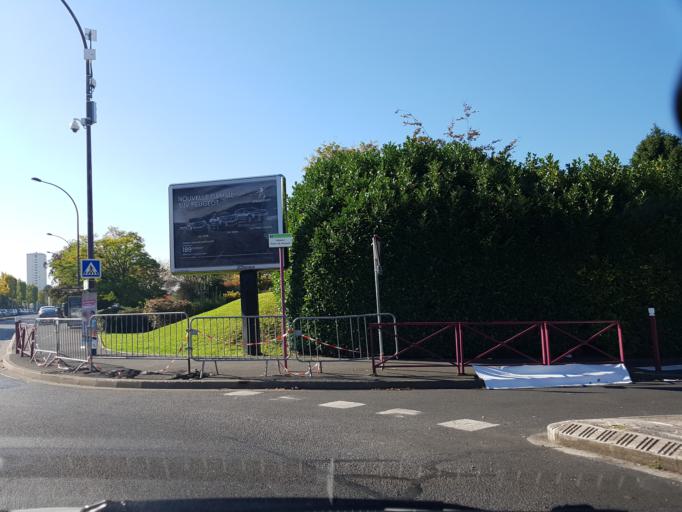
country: FR
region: Ile-de-France
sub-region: Departement des Hauts-de-Seine
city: Bourg-la-Reine
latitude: 48.7734
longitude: 2.3238
